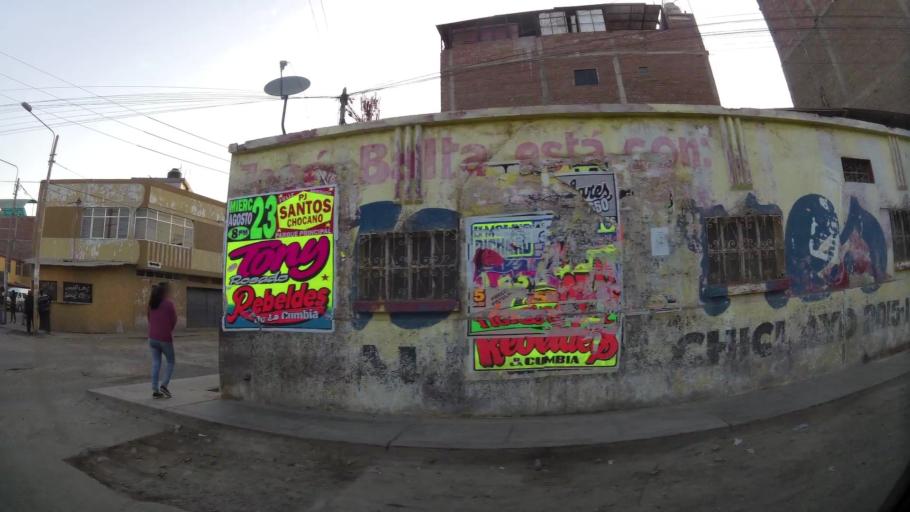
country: PE
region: Lambayeque
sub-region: Provincia de Chiclayo
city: Santa Rosa
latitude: -6.7656
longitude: -79.8333
